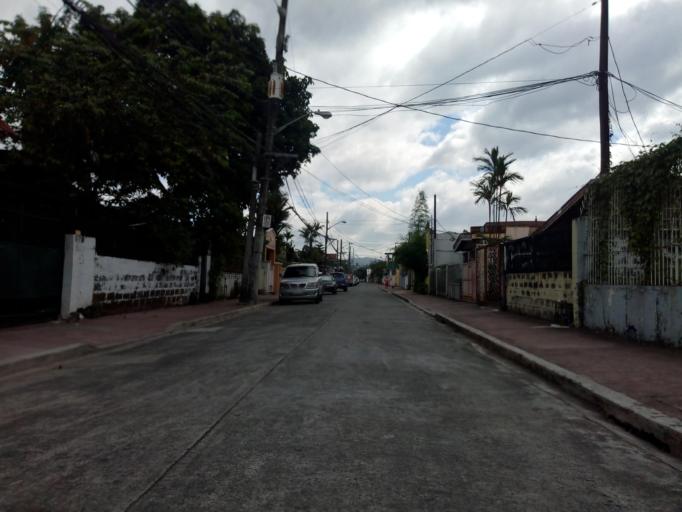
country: PH
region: Calabarzon
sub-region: Province of Rizal
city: Antipolo
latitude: 14.6387
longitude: 121.1174
